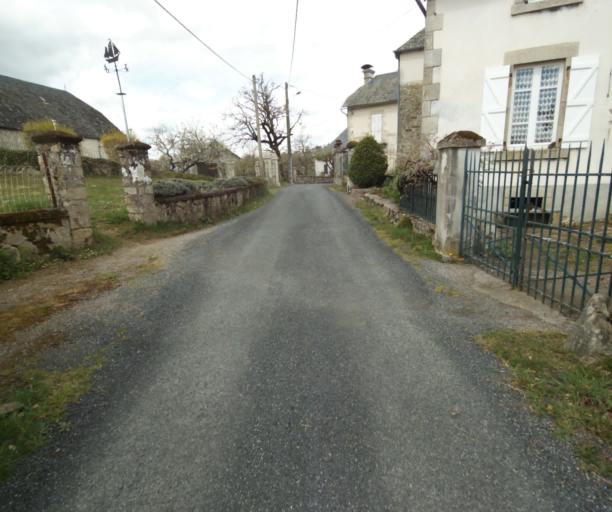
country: FR
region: Limousin
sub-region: Departement de la Correze
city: Sainte-Fortunade
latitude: 45.1896
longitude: 1.8626
